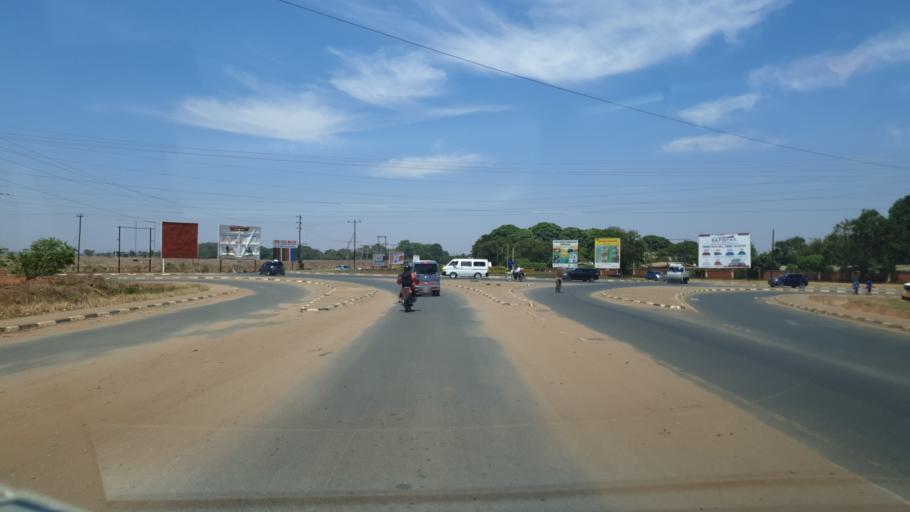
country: MW
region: Central Region
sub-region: Lilongwe District
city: Lilongwe
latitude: -13.9749
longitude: 33.7406
